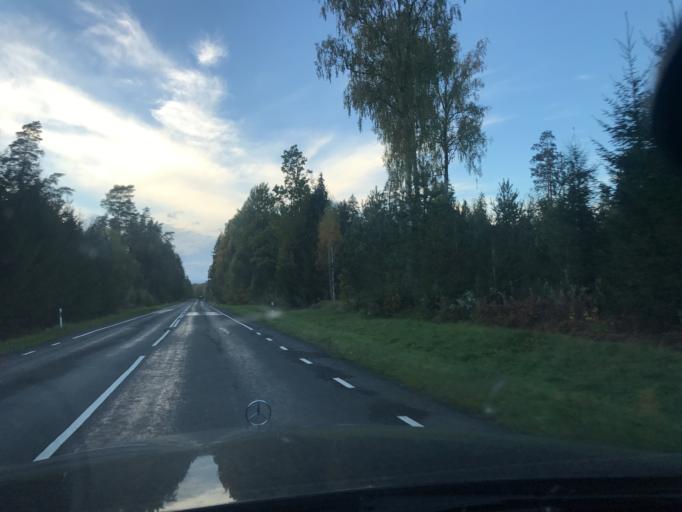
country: EE
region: Vorumaa
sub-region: Antsla vald
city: Vana-Antsla
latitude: 57.8751
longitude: 26.5877
